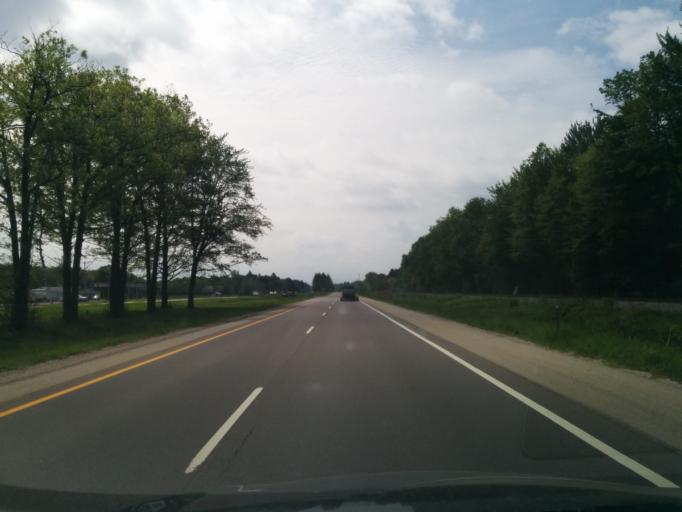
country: US
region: Michigan
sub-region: Ottawa County
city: Grand Haven
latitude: 42.9909
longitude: -86.1952
